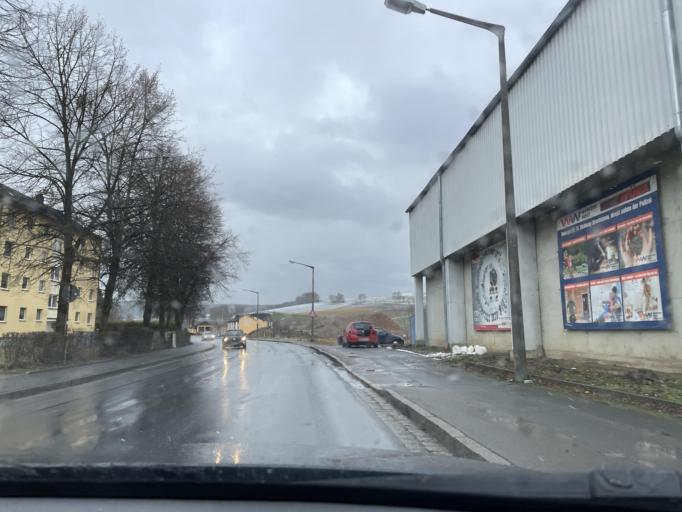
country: DE
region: Bavaria
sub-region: Upper Palatinate
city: Furth im Wald
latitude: 49.3042
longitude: 12.8503
